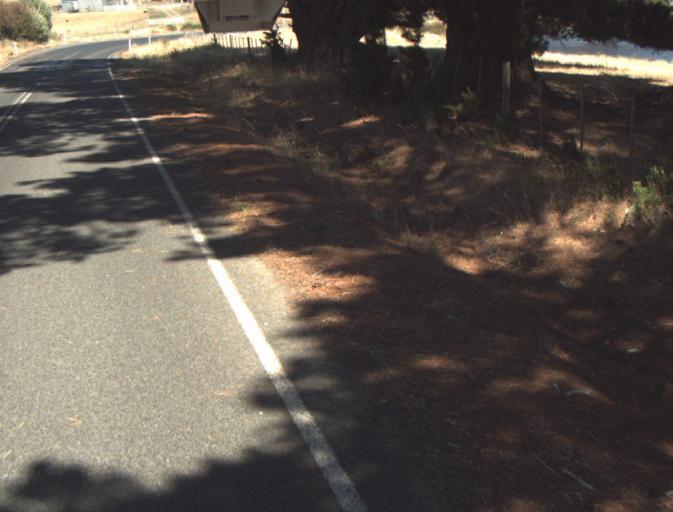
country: AU
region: Tasmania
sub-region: Launceston
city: Newstead
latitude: -41.3265
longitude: 147.3568
